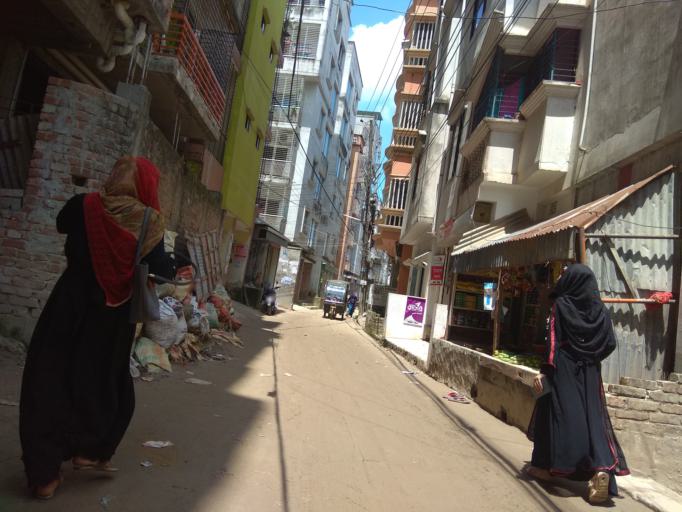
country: BD
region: Dhaka
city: Tungi
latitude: 23.8305
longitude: 90.3866
